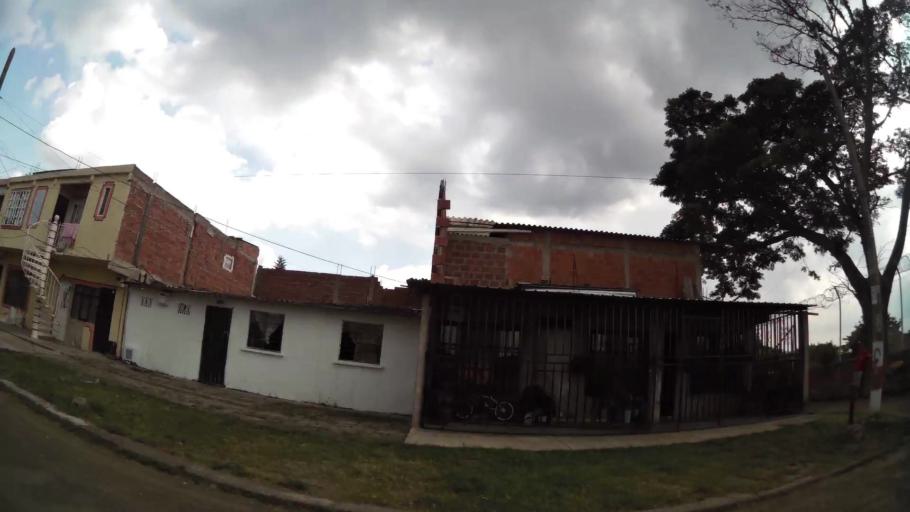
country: CO
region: Valle del Cauca
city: Cali
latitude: 3.4588
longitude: -76.4899
